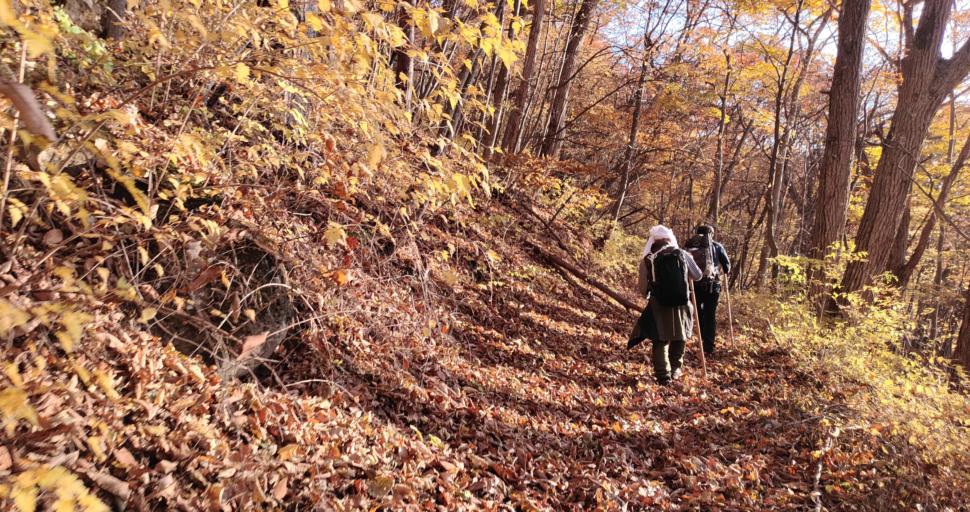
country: JP
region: Nagano
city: Komoro
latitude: 36.3827
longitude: 138.4381
